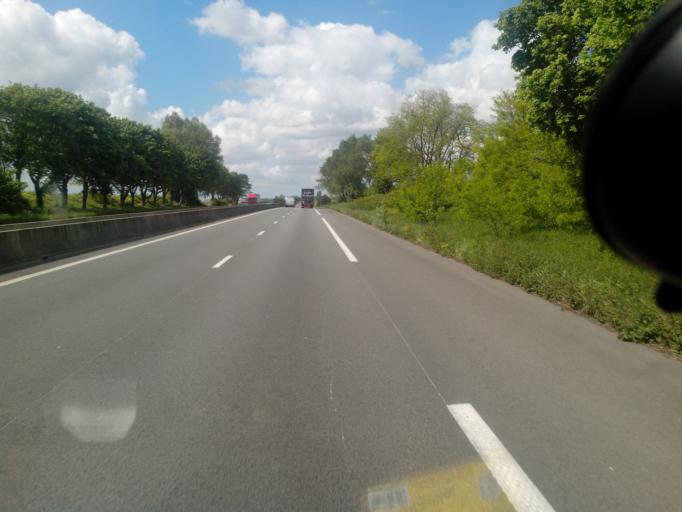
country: FR
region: Nord-Pas-de-Calais
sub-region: Departement du Nord
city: Godewaersvelde
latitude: 50.7673
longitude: 2.6376
